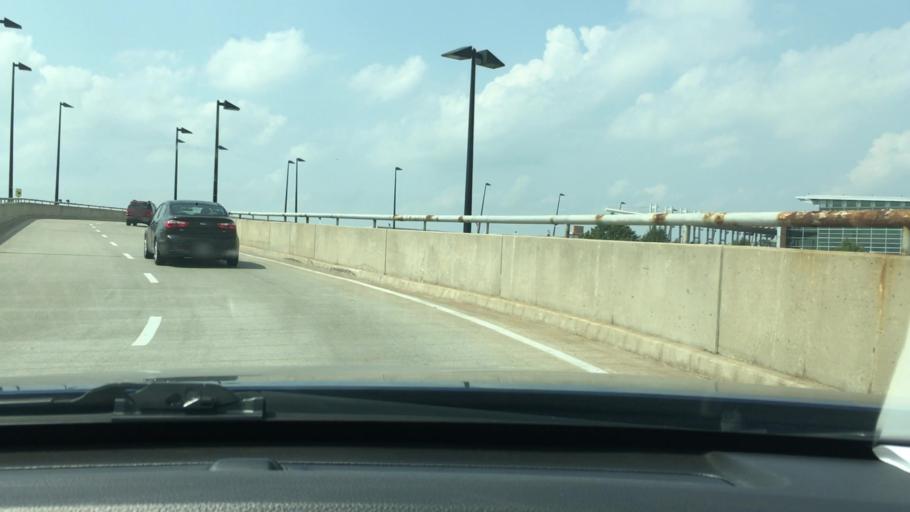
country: US
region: Illinois
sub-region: Cook County
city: Hometown
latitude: 41.7862
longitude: -87.7400
